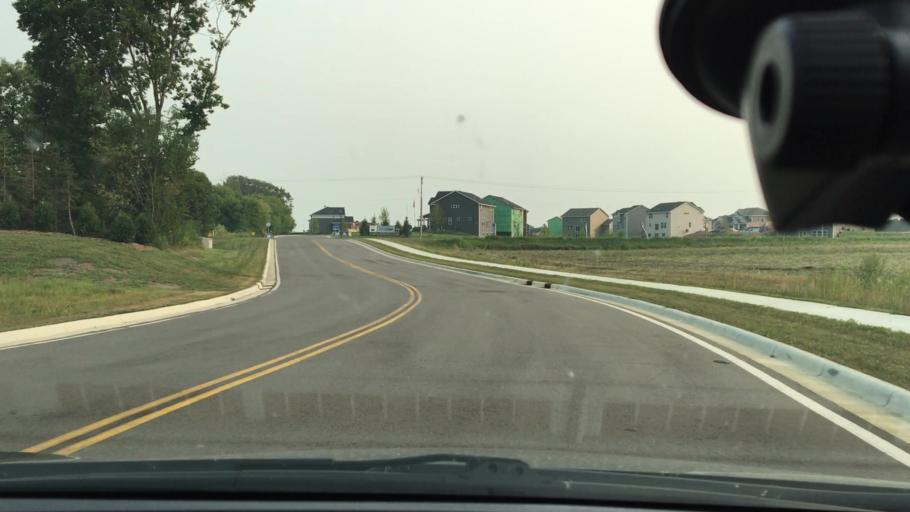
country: US
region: Minnesota
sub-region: Wright County
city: Saint Michael
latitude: 45.2115
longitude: -93.6291
